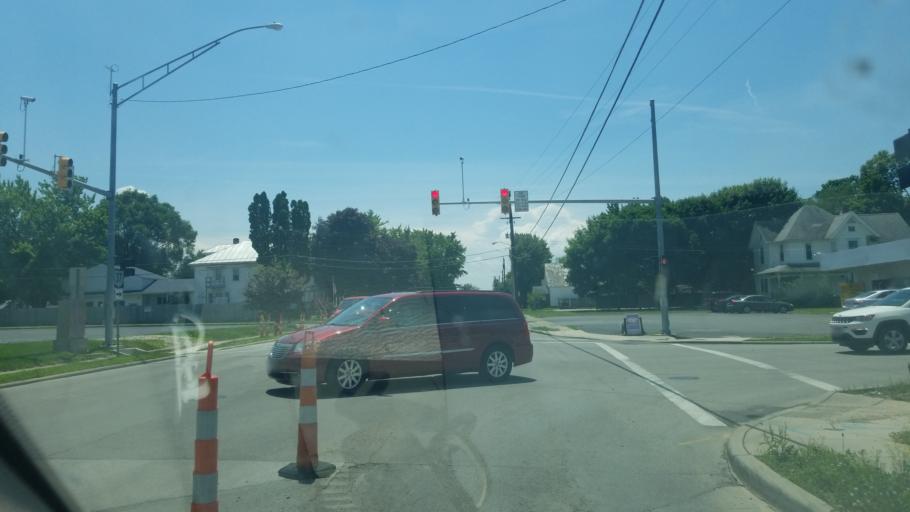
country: US
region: Ohio
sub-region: Hancock County
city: Findlay
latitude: 41.0345
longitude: -83.6412
